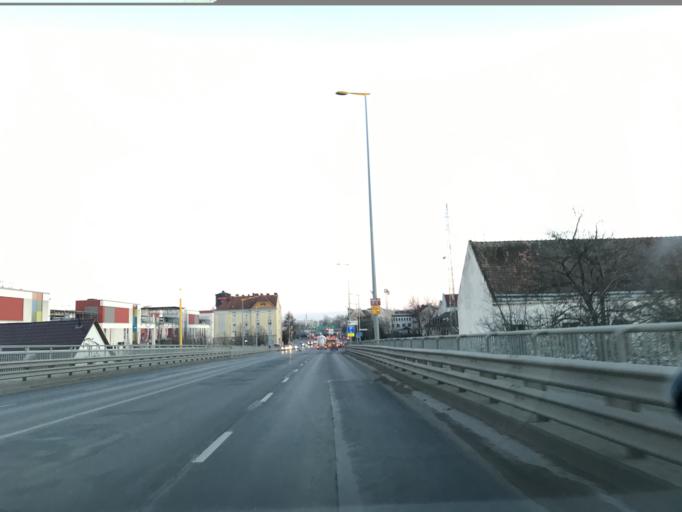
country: HU
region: Gyor-Moson-Sopron
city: Gyor
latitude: 47.6918
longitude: 17.6414
